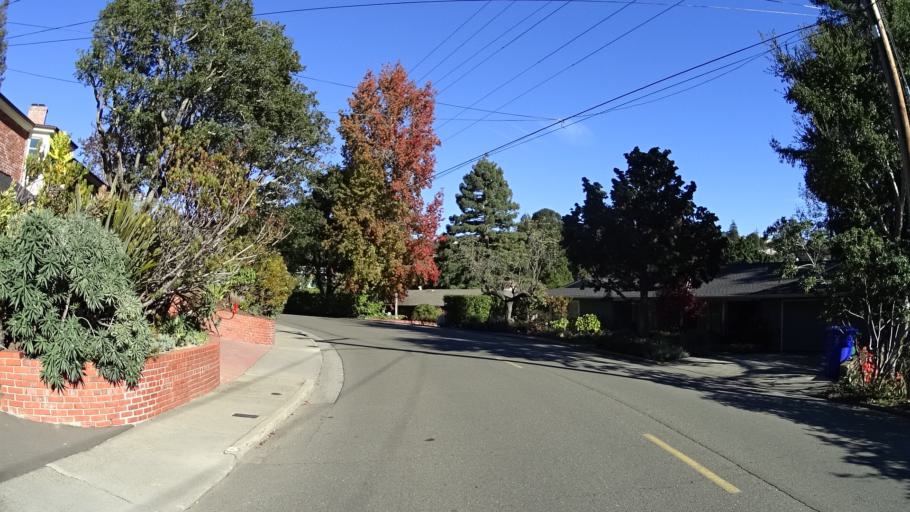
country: US
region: California
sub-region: Alameda County
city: Piedmont
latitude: 37.8158
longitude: -122.2207
